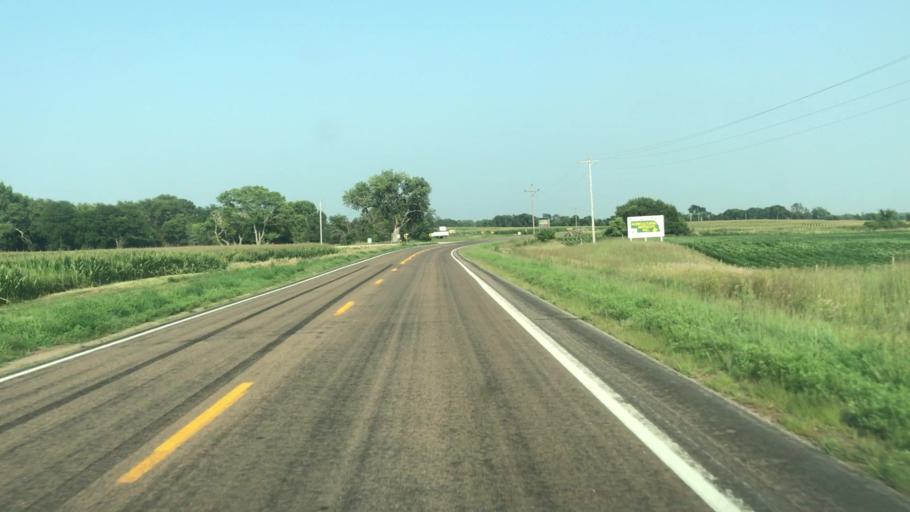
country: US
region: Nebraska
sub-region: Buffalo County
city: Ravenna
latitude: 41.0757
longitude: -98.7319
